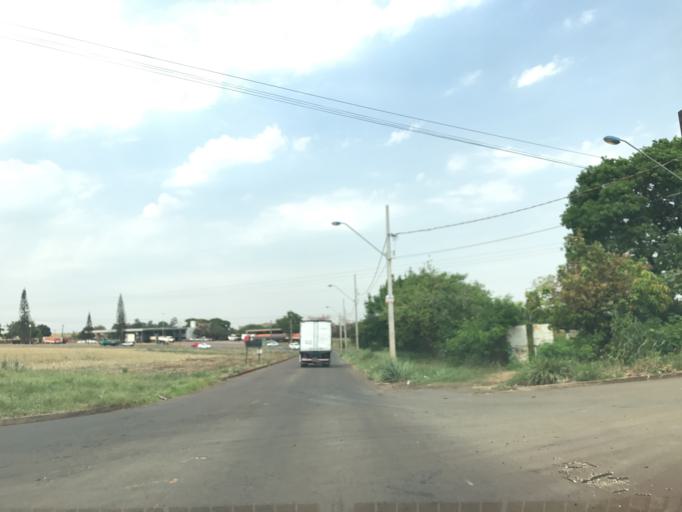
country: BR
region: Parana
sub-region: Maringa
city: Maringa
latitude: -23.4564
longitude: -51.9529
